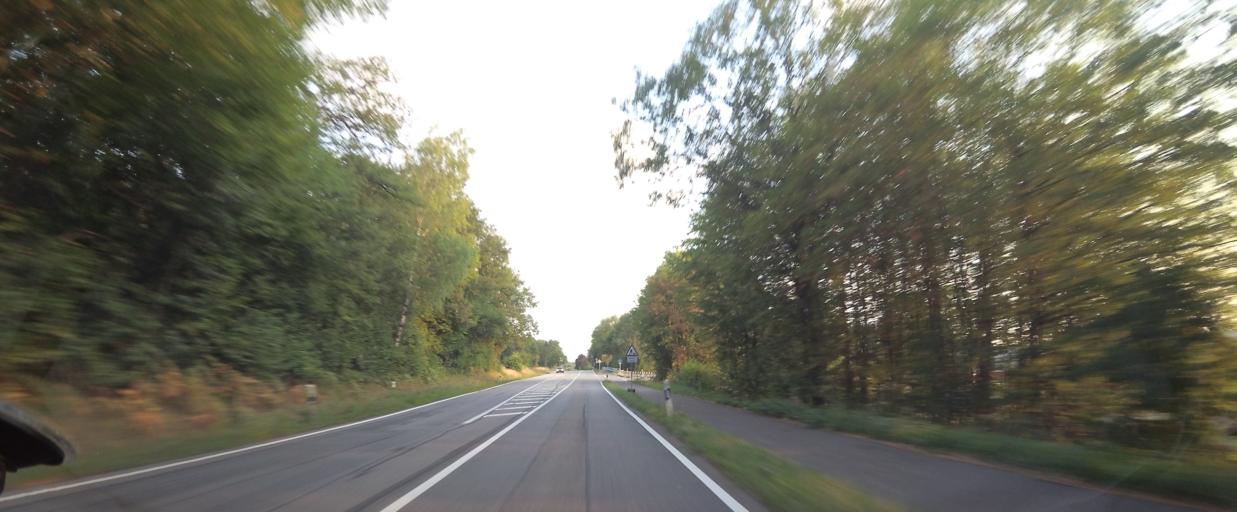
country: DE
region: Saarland
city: Wadern
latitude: 49.5468
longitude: 6.9019
